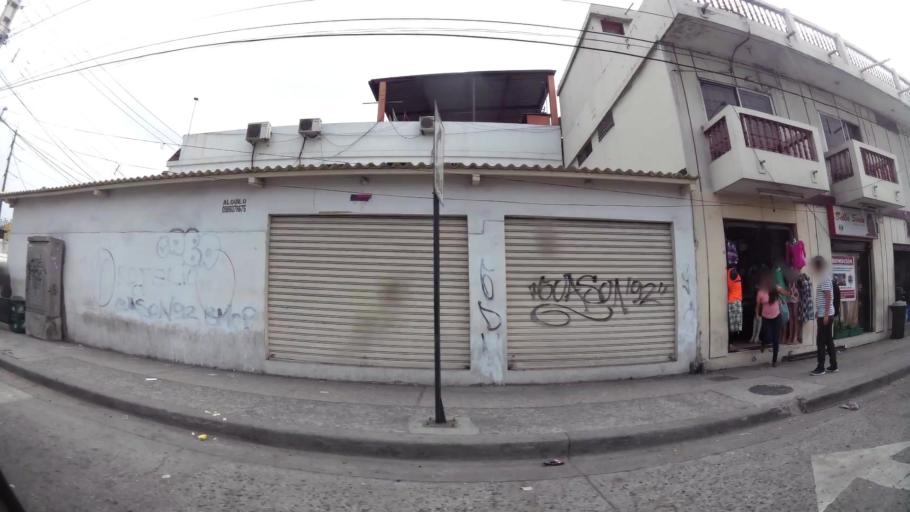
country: EC
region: Guayas
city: Eloy Alfaro
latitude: -2.1388
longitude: -79.8840
